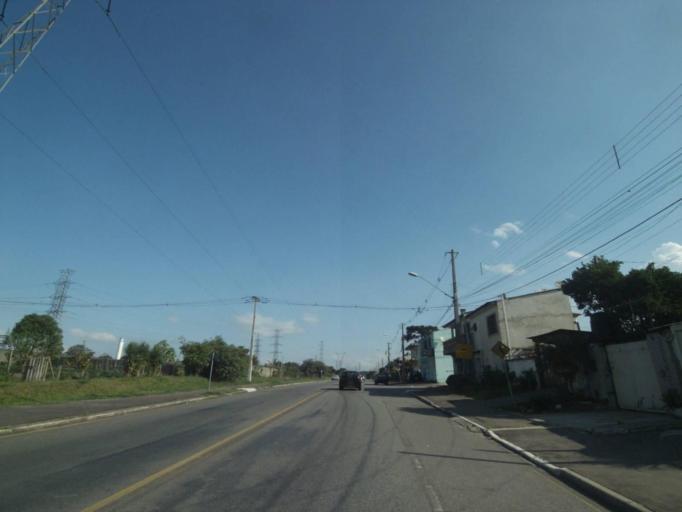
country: BR
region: Parana
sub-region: Araucaria
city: Araucaria
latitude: -25.5258
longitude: -49.3340
